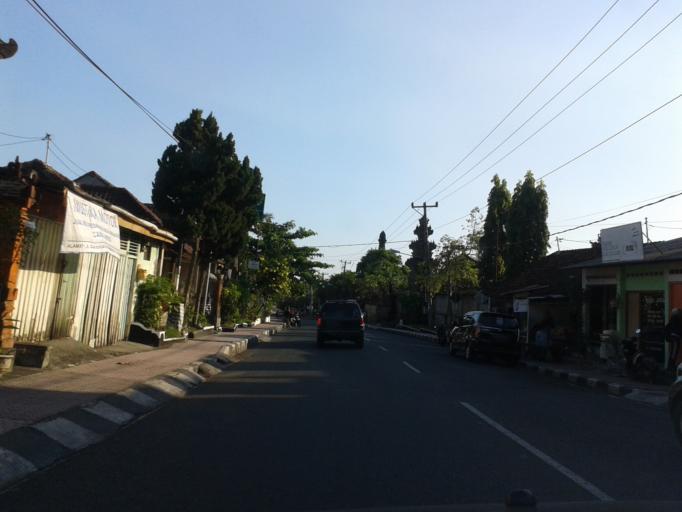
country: ID
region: Bali
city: Semarapura
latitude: -8.5330
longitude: 115.4040
